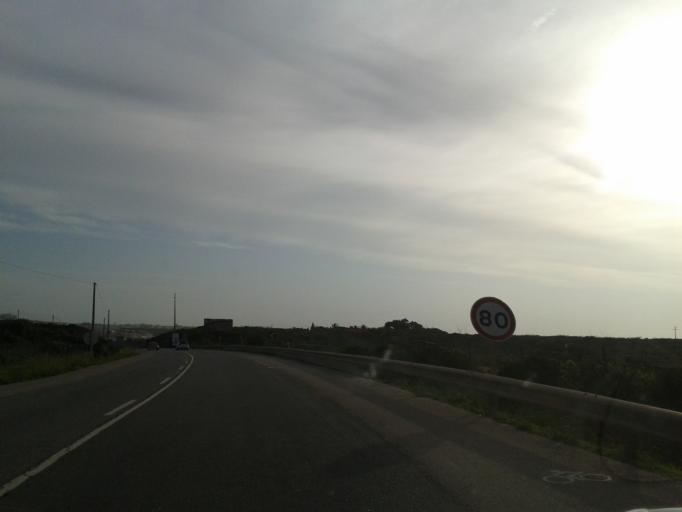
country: PT
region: Faro
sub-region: Vila do Bispo
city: Sagres
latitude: 37.0255
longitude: -8.9377
